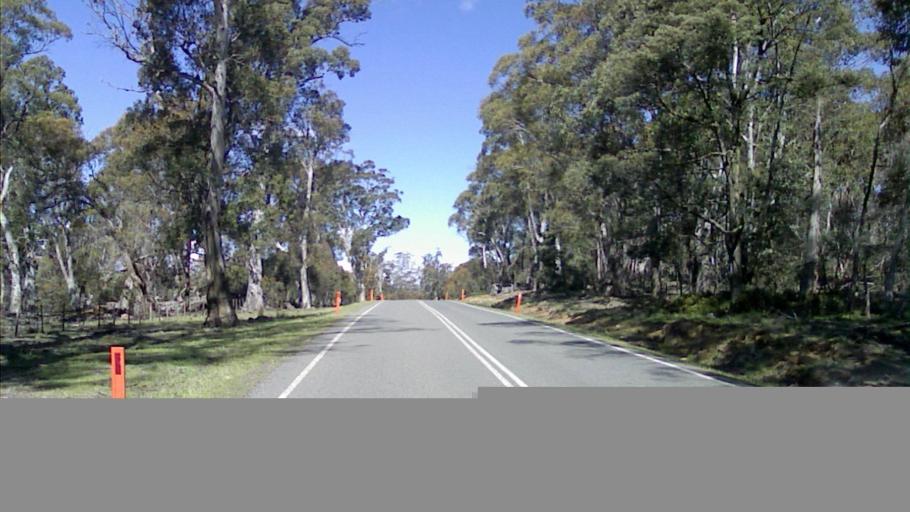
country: AU
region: Tasmania
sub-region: Meander Valley
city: Westbury
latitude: -42.0251
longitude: 146.8143
